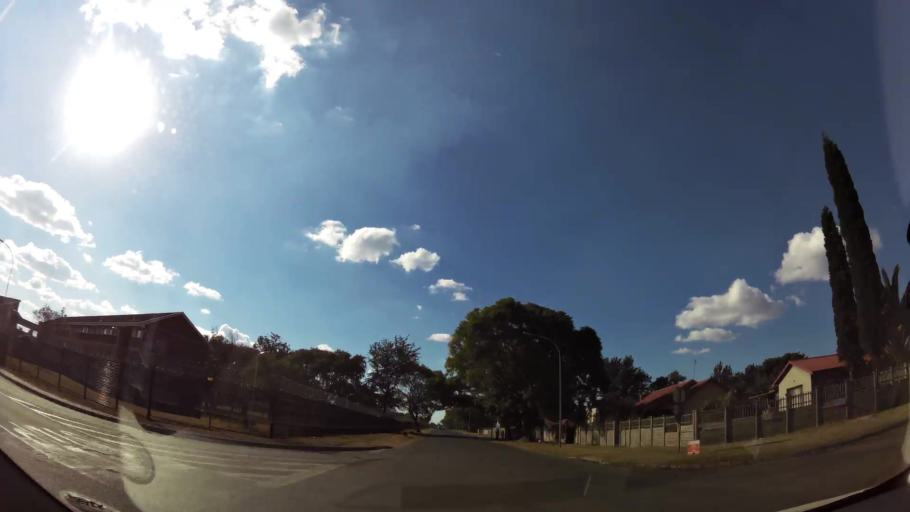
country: ZA
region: Mpumalanga
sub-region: Nkangala District Municipality
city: Witbank
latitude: -25.8911
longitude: 29.2207
